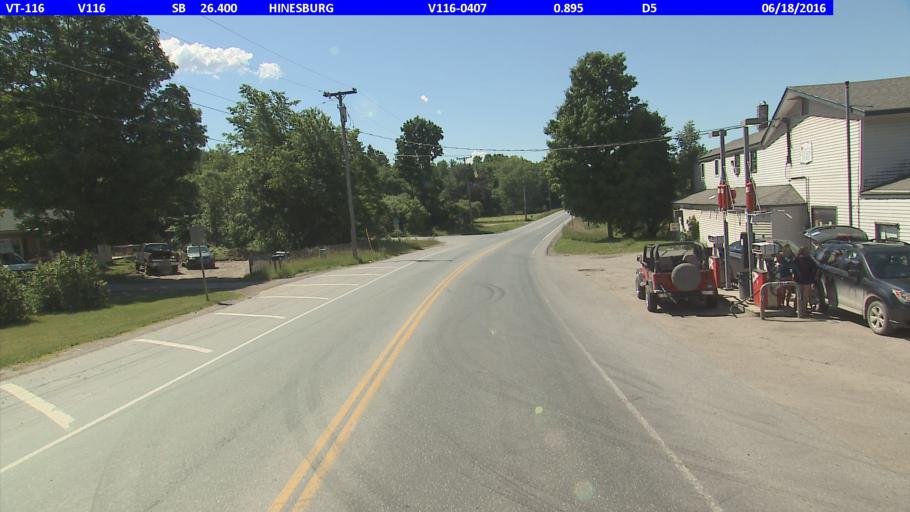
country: US
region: Vermont
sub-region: Chittenden County
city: Hinesburg
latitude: 44.2929
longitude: -73.0706
